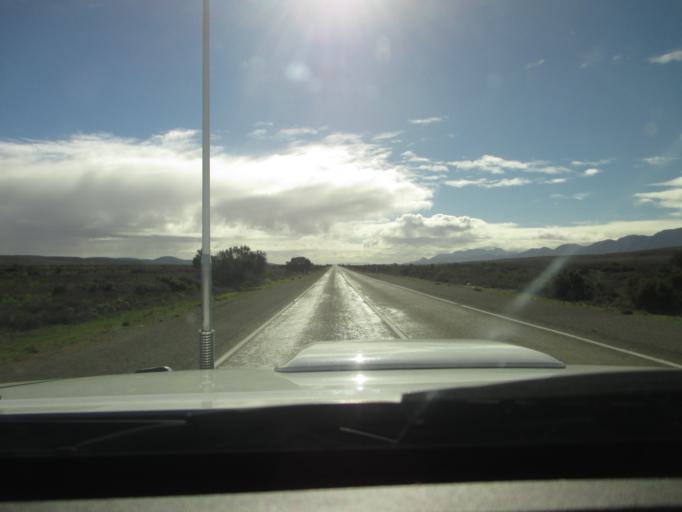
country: AU
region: South Australia
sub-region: Flinders Ranges
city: Quorn
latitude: -31.7213
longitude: 138.3474
